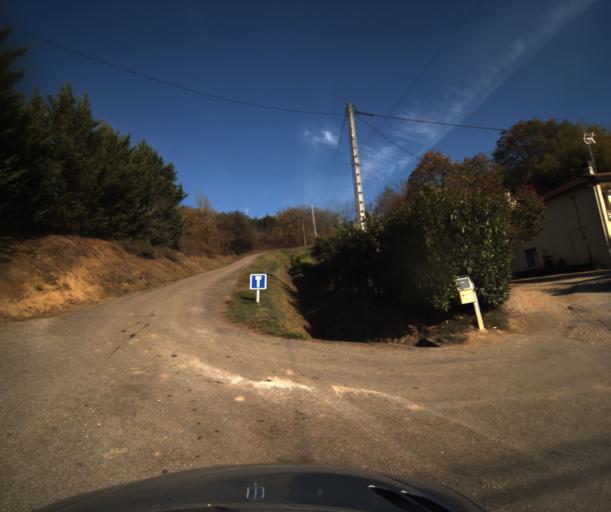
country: FR
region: Midi-Pyrenees
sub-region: Departement du Tarn-et-Garonne
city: Lafrancaise
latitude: 44.1012
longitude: 1.2981
